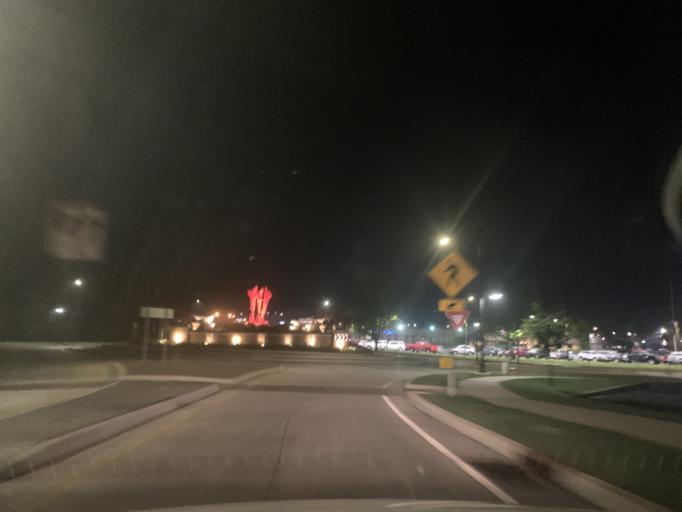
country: US
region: Indiana
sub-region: Saint Joseph County
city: Gulivoire Park
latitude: 41.6367
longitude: -86.2503
